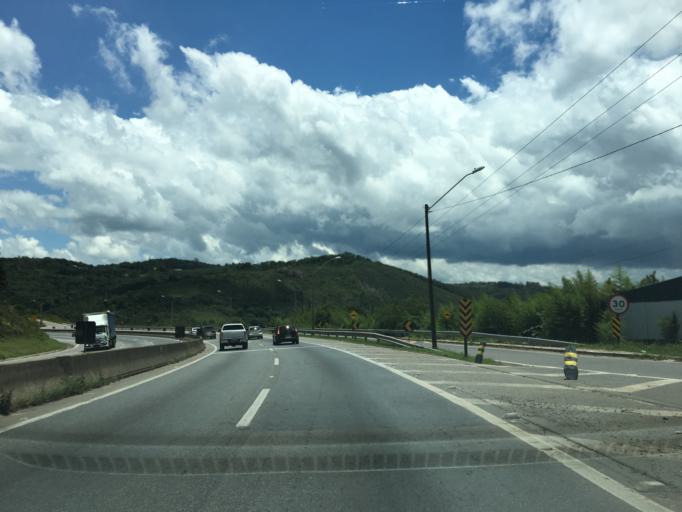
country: BR
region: Sao Paulo
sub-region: Mairipora
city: Mairipora
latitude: -23.2849
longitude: -46.5899
